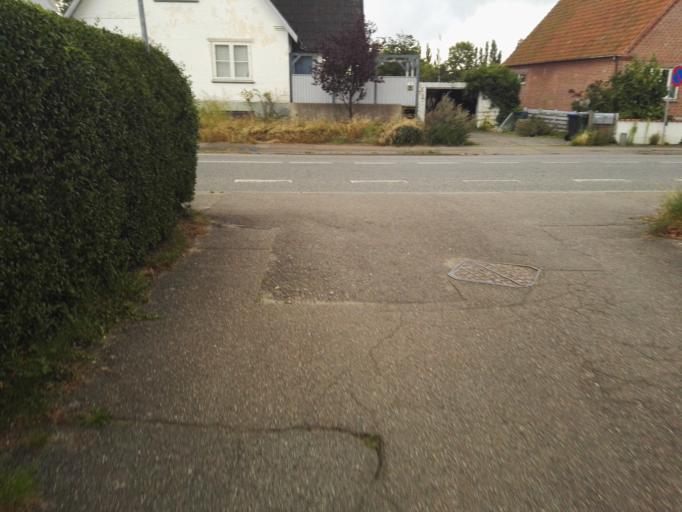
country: DK
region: Zealand
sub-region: Odsherred Kommune
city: Nykobing Sjaelland
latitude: 55.9188
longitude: 11.6689
